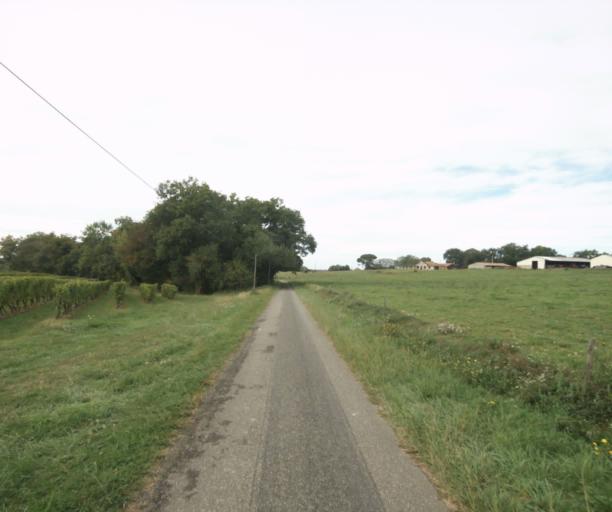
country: FR
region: Midi-Pyrenees
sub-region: Departement du Gers
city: Cazaubon
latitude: 43.8851
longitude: -0.1355
